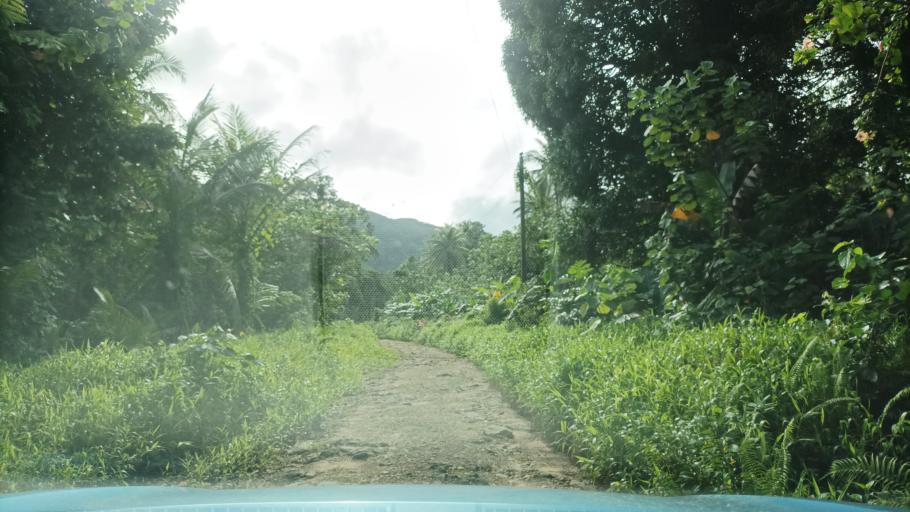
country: FM
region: Pohnpei
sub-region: Kolonia Municipality
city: Kolonia
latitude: 6.9301
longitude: 158.2397
